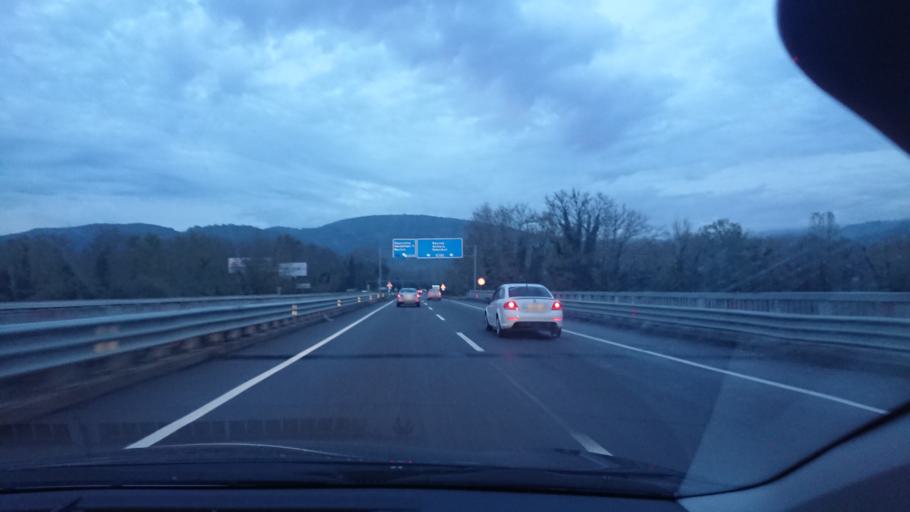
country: TR
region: Zonguldak
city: Gokcebey
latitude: 41.3367
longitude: 32.0831
